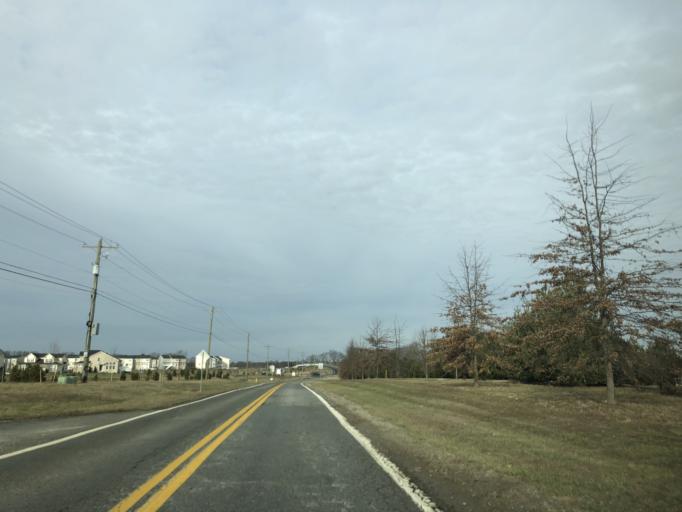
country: US
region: Delaware
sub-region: New Castle County
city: Delaware City
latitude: 39.5198
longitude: -75.6568
